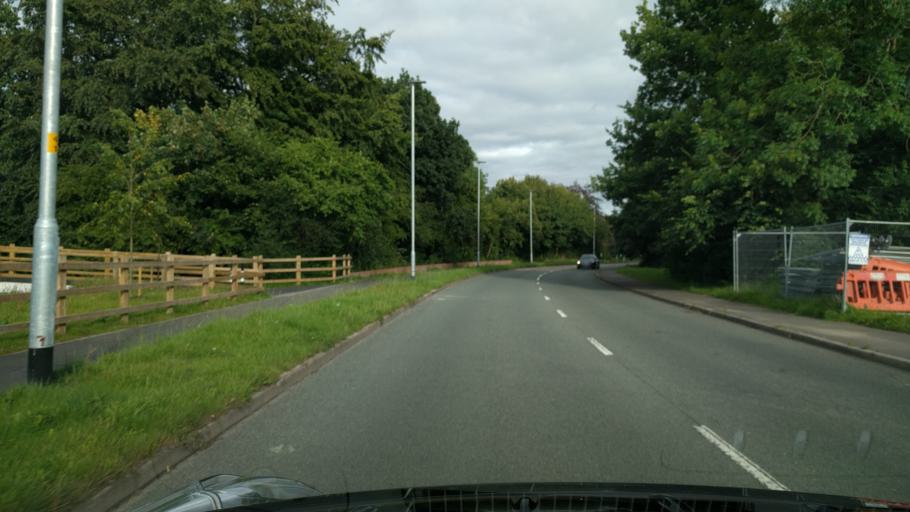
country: GB
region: England
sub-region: Warrington
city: Croft
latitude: 53.4217
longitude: -2.5584
